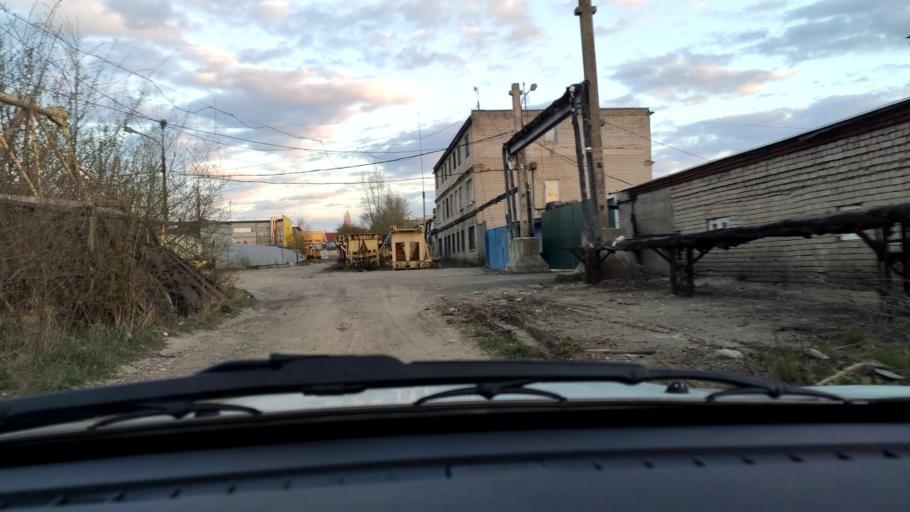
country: RU
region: Voronezj
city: Voronezh
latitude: 51.6862
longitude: 39.1457
